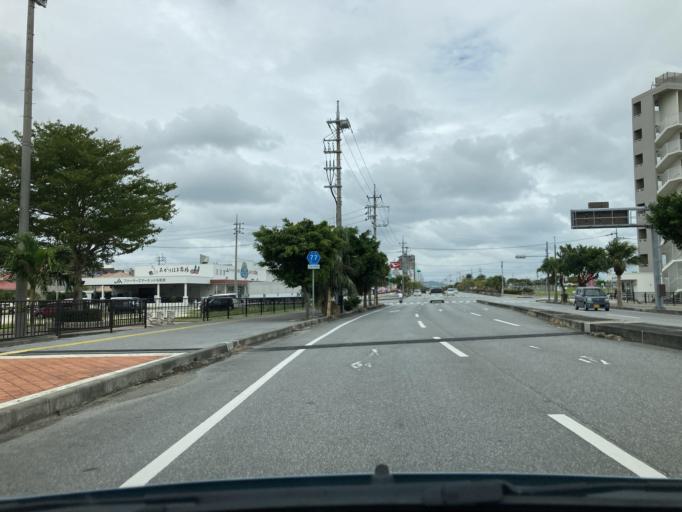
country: JP
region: Okinawa
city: Ginowan
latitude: 26.2029
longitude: 127.7606
